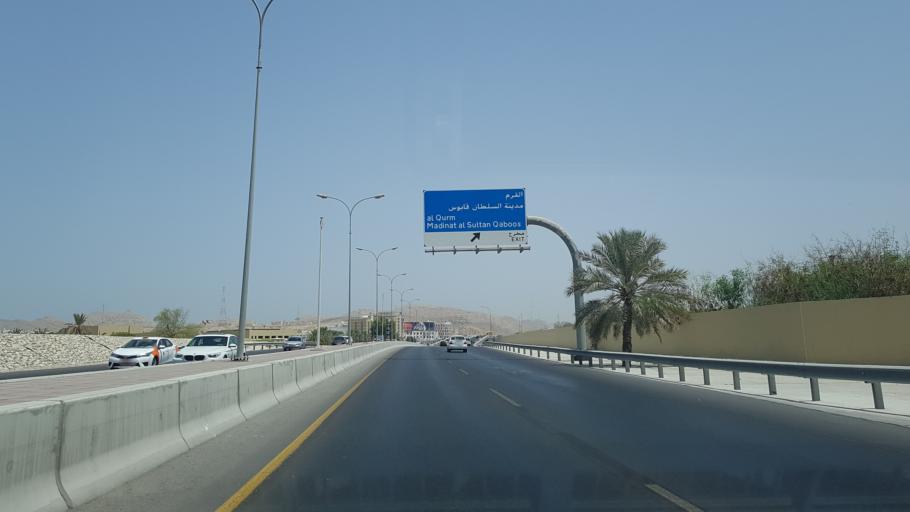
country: OM
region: Muhafazat Masqat
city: Bawshar
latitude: 23.6138
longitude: 58.4866
